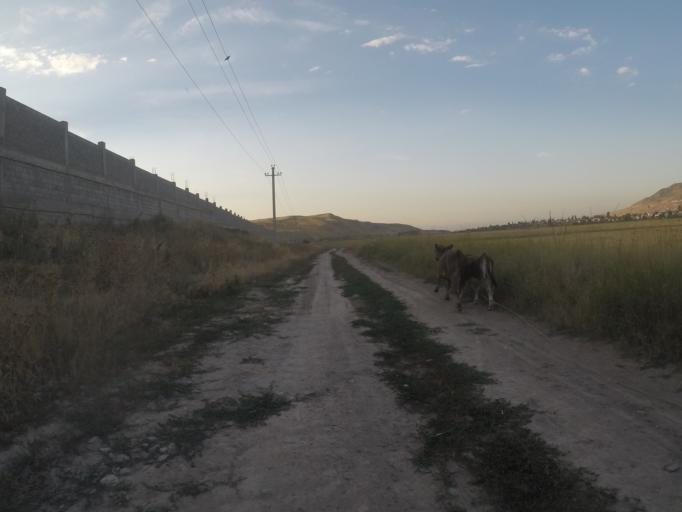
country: KG
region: Chuy
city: Bishkek
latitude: 42.7533
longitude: 74.6366
